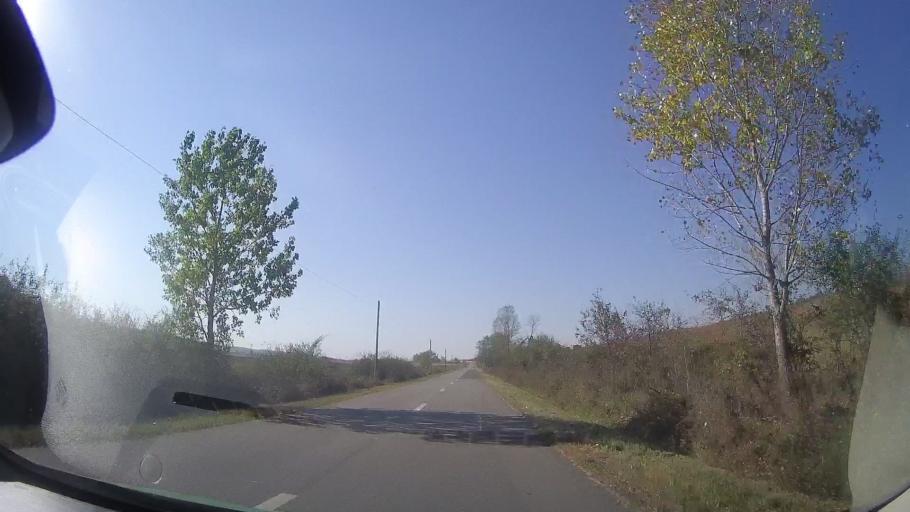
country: RO
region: Timis
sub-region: Comuna Secas
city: Secas
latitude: 45.8697
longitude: 21.8116
